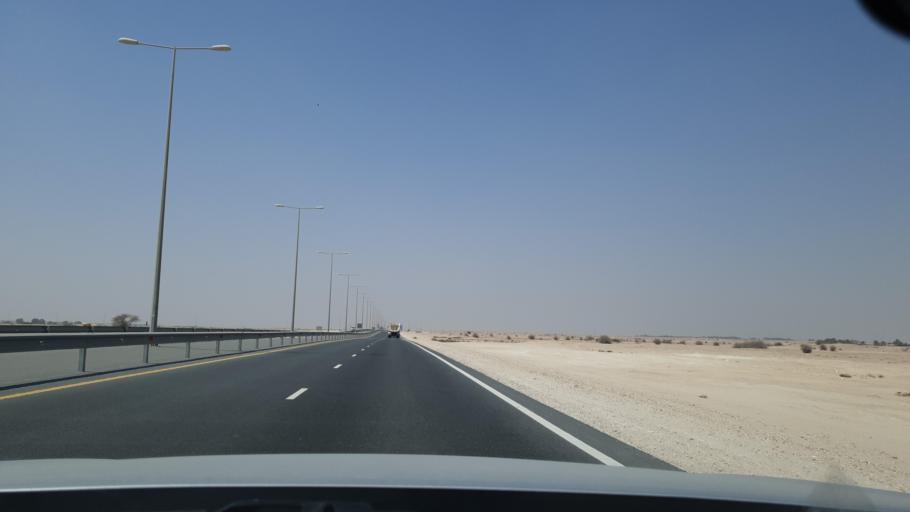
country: QA
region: Baladiyat az Za`ayin
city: Az Za`ayin
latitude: 25.6213
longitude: 51.3488
